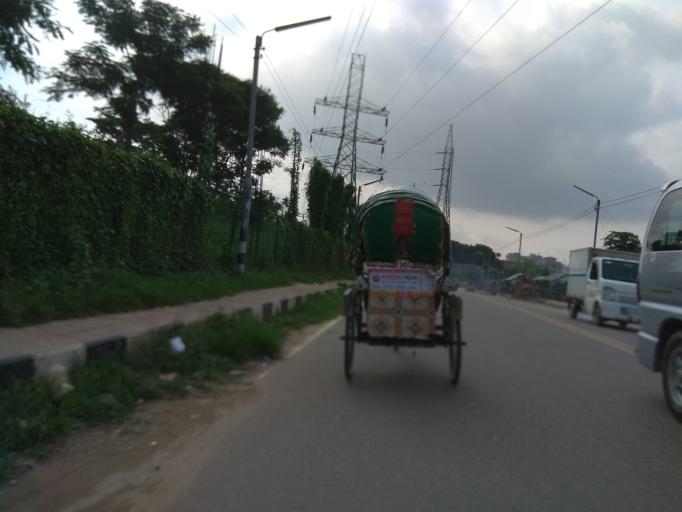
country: BD
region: Dhaka
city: Tungi
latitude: 23.8302
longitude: 90.3582
